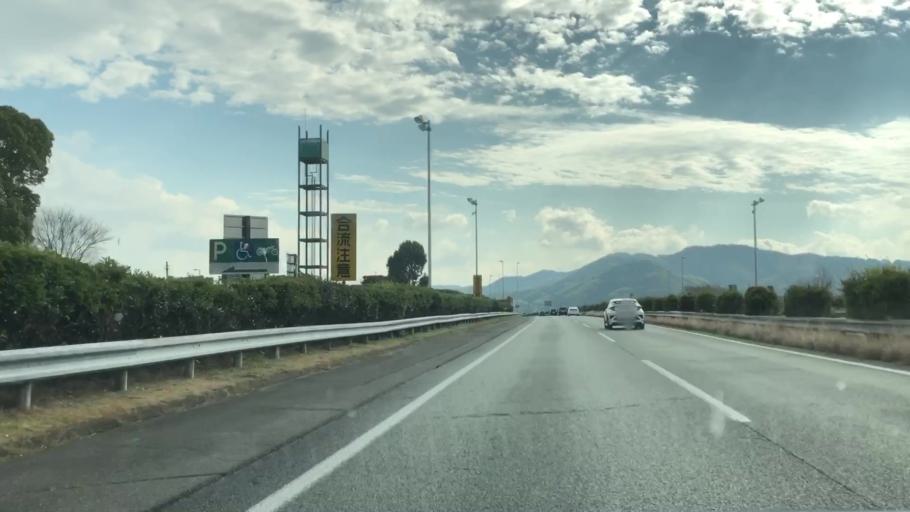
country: JP
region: Fukuoka
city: Setakamachi-takayanagi
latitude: 33.1289
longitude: 130.5177
